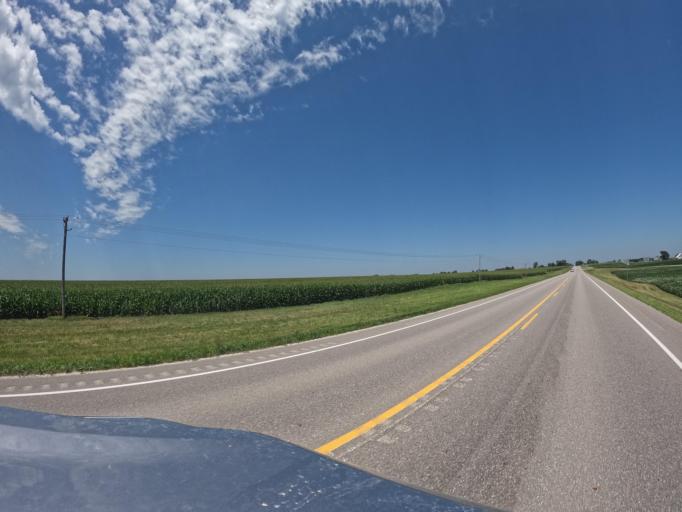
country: US
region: Iowa
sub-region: Keokuk County
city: Sigourney
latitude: 41.4184
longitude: -92.3550
